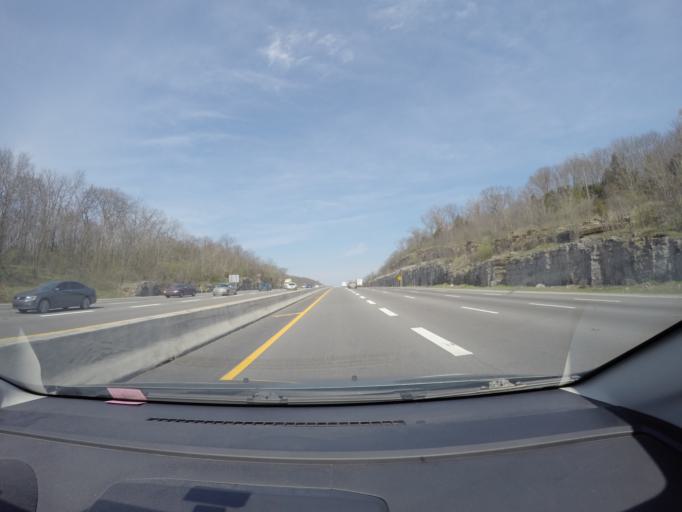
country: US
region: Tennessee
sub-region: Rutherford County
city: La Vergne
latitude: 36.0208
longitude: -86.6275
